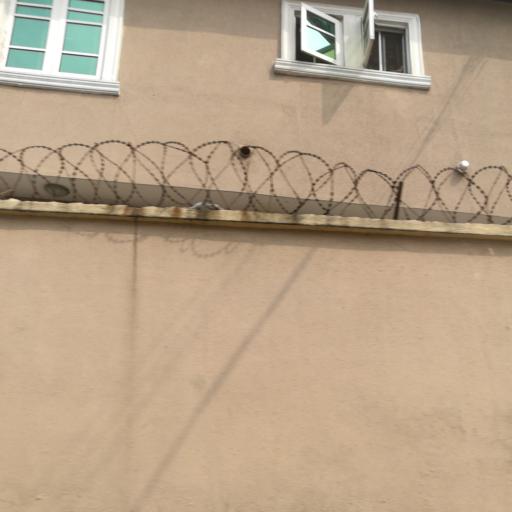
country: NG
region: Rivers
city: Port Harcourt
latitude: 4.8372
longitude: 7.0659
